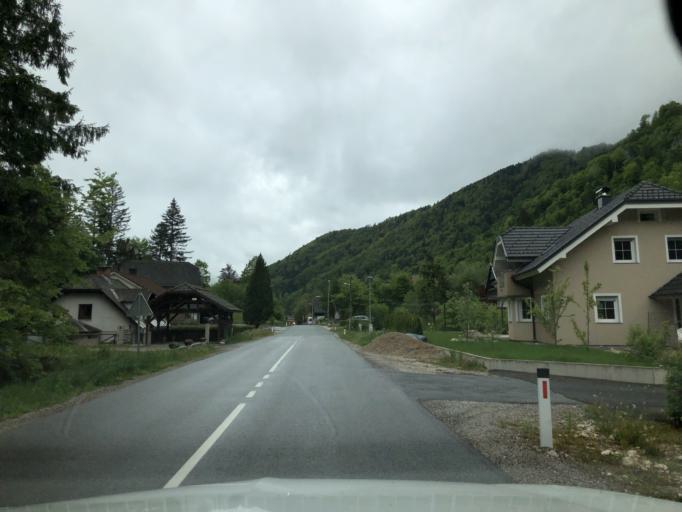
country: SI
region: Jesenice
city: Slovenski Javornik
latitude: 46.4177
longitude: 14.0827
